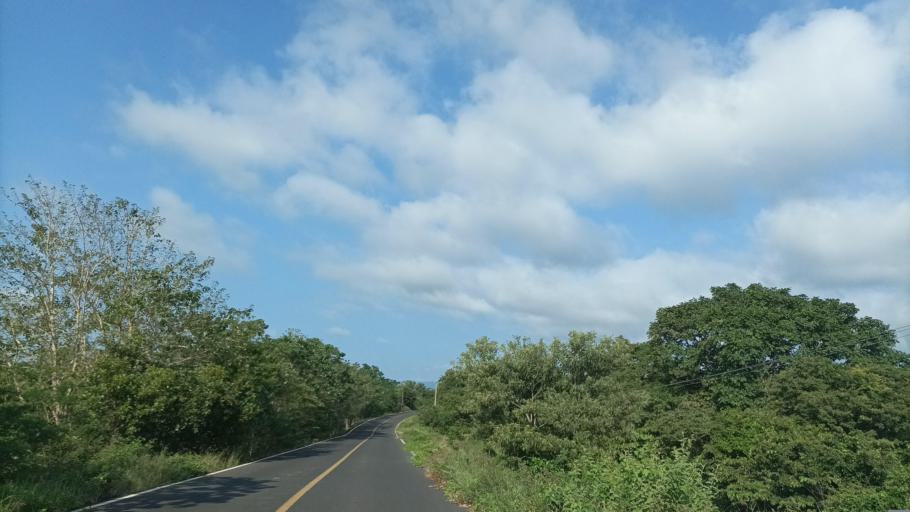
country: MX
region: Veracruz
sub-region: Chinameca
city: Chacalapa
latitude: 18.1651
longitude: -94.6588
